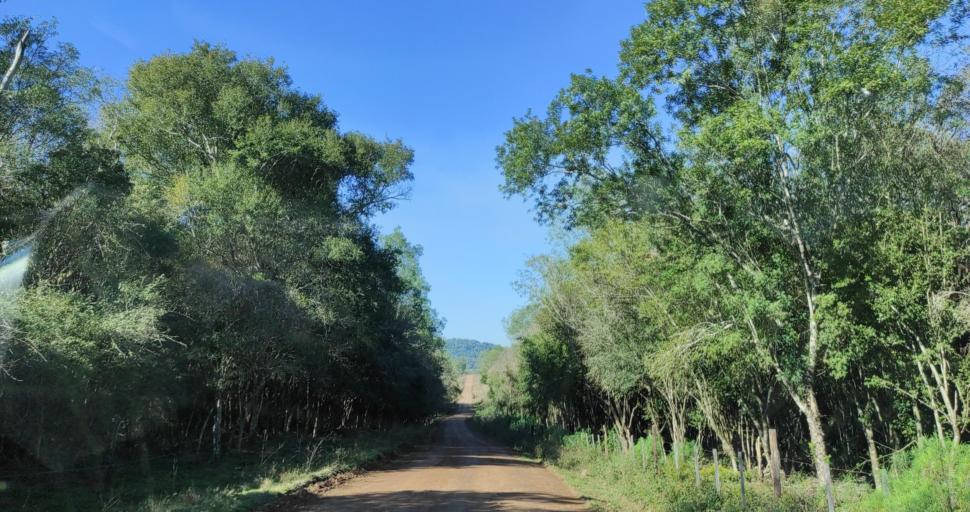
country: AR
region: Misiones
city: Cerro Cora
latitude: -27.6387
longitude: -55.6677
